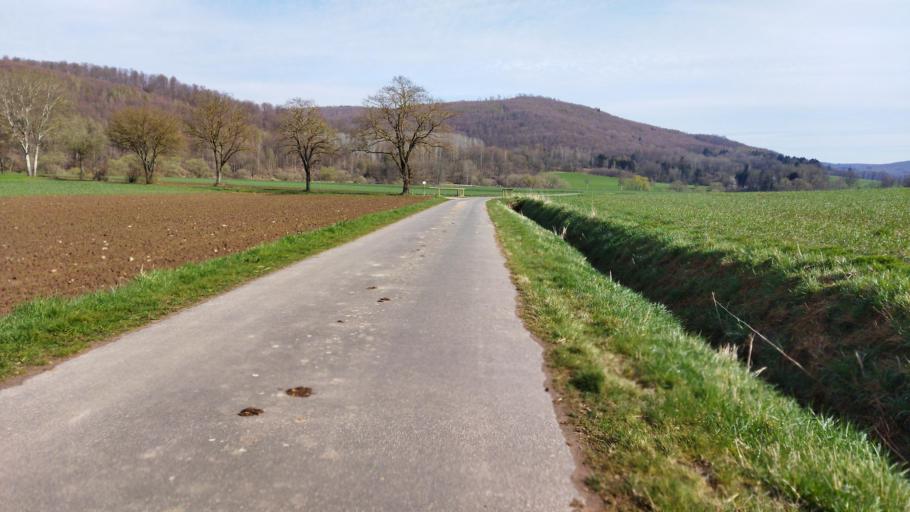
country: DE
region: Lower Saxony
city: Buhren
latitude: 51.5186
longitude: 9.5900
